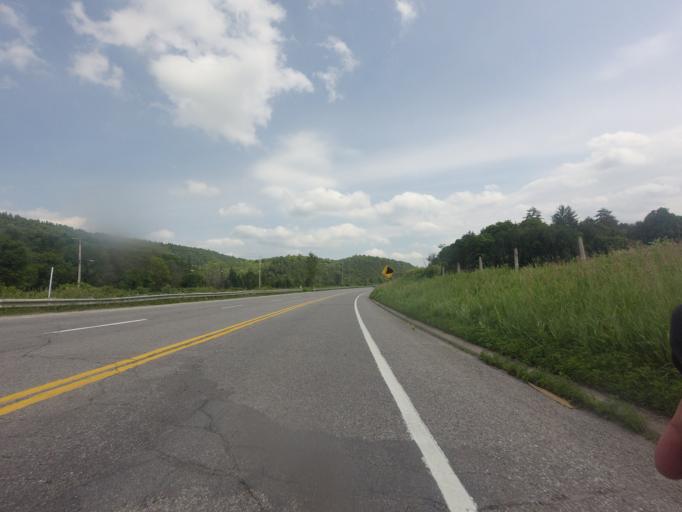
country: CA
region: Quebec
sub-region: Outaouais
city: Wakefield
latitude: 45.7595
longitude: -75.9211
